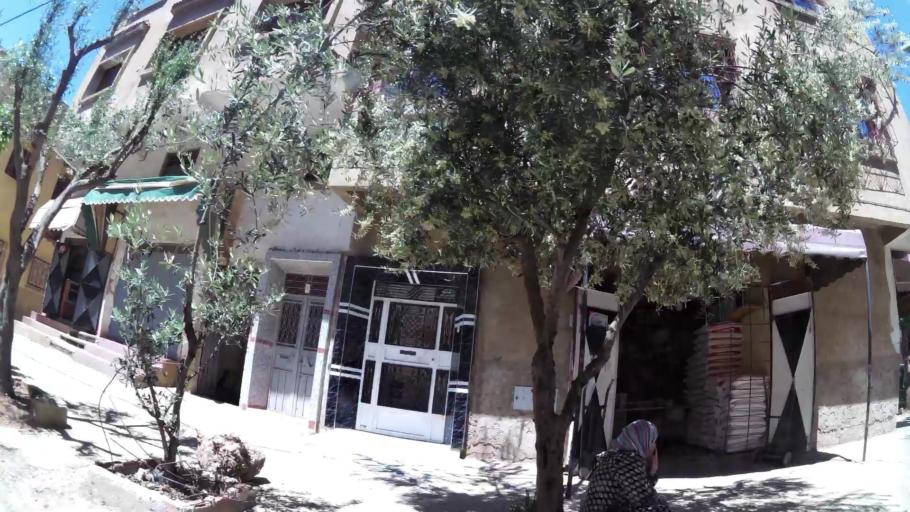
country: MA
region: Meknes-Tafilalet
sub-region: Meknes
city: Meknes
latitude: 33.9056
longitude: -5.5769
